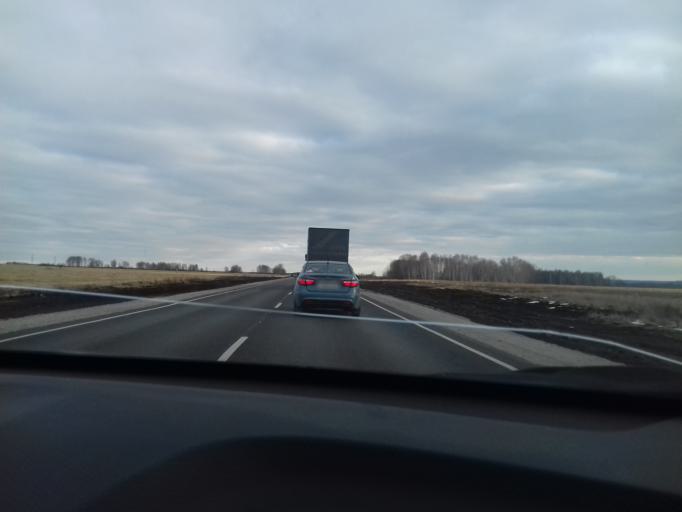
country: RU
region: Kurgan
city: Kataysk
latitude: 56.2923
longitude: 62.6823
